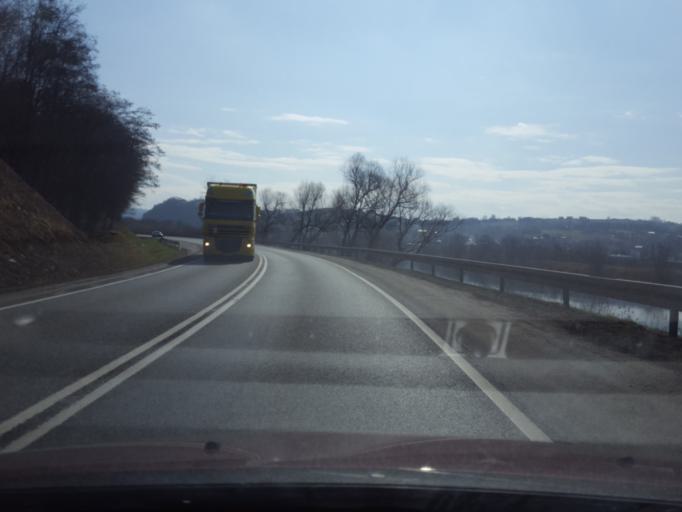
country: PL
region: Lesser Poland Voivodeship
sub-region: Powiat nowosadecki
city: Chelmiec
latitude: 49.6772
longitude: 20.6548
